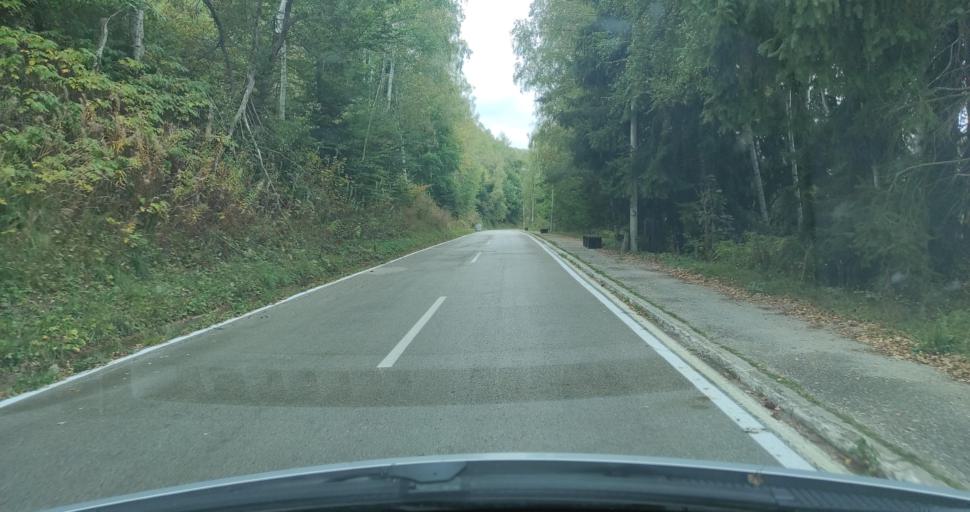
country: RS
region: Central Serbia
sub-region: Jablanicki Okrug
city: Crna Trava
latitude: 42.7444
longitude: 22.3265
